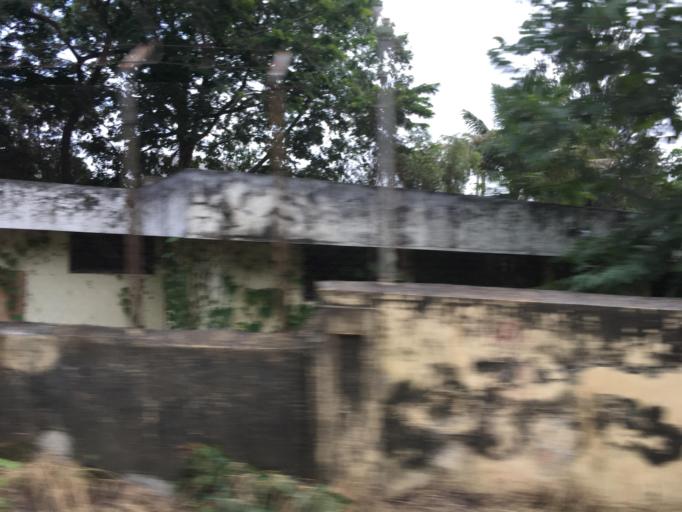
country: GT
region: Guatemala
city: Amatitlan
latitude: 14.4613
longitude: -90.5815
